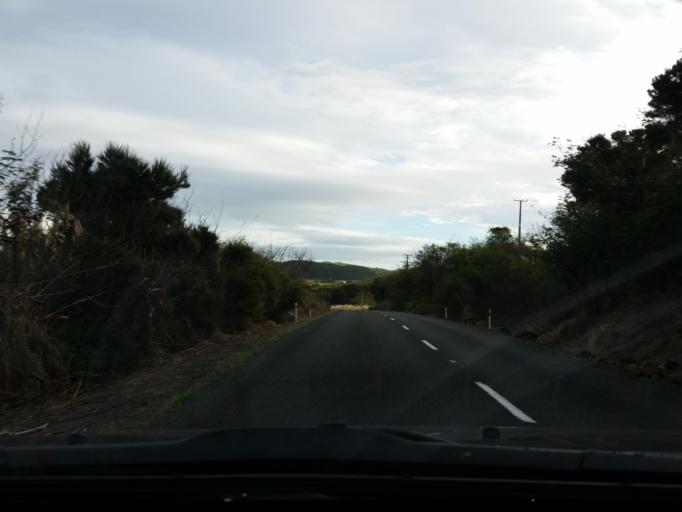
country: NZ
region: Northland
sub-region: Kaipara District
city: Dargaville
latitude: -35.8279
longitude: 173.6711
